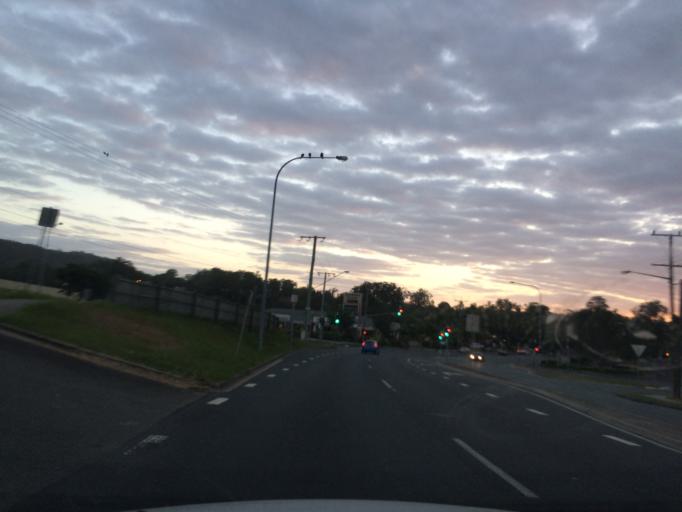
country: AU
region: Queensland
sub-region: Brisbane
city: Kenmore Hills
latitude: -27.5080
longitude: 152.9471
